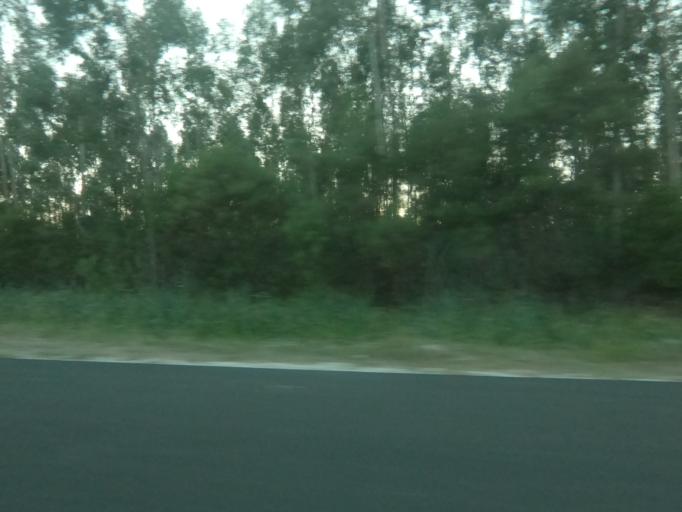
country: PT
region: Leiria
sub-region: Pombal
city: Pombal
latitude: 39.8735
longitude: -8.7026
